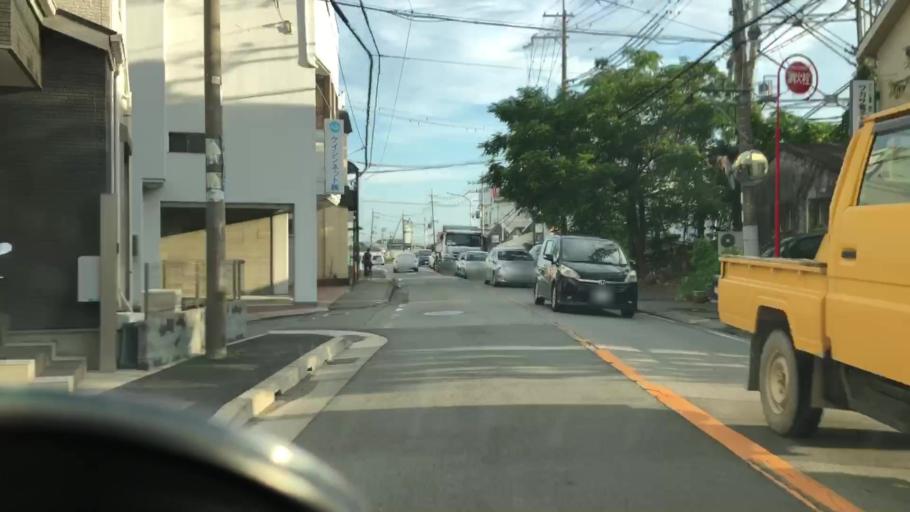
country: JP
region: Hyogo
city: Takarazuka
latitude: 34.7872
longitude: 135.3689
